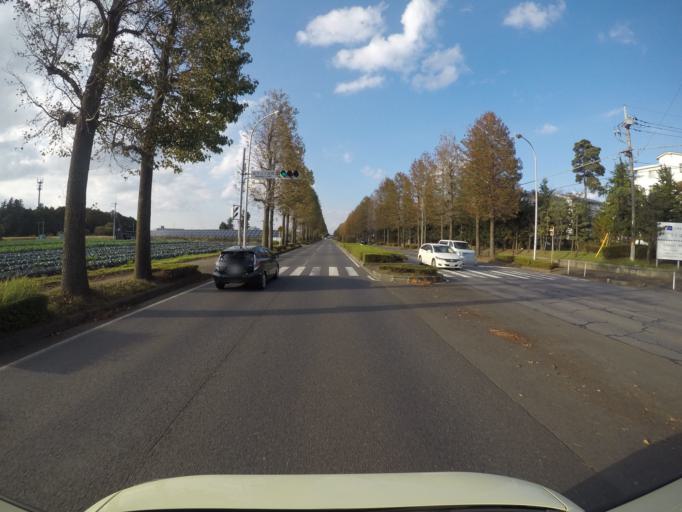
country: JP
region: Ibaraki
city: Naka
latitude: 36.0660
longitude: 140.1004
